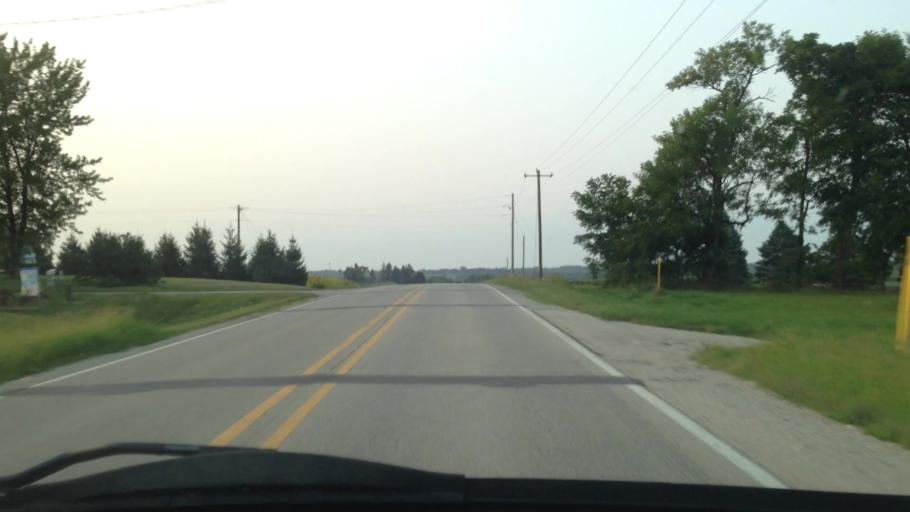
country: US
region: Iowa
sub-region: Linn County
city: Palo
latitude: 42.0789
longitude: -91.8690
